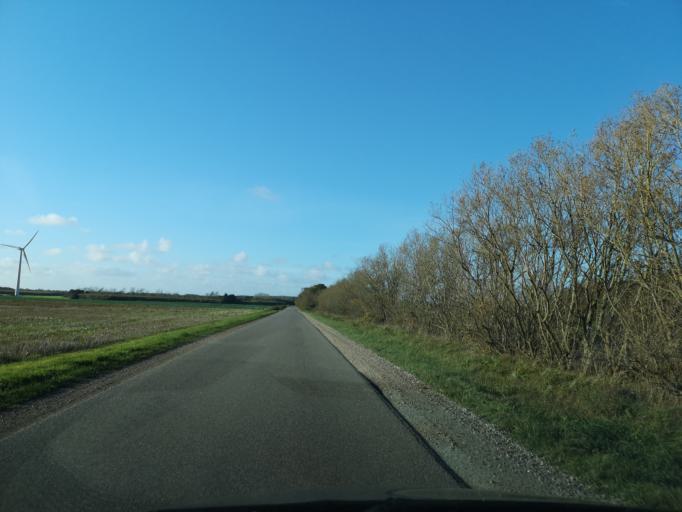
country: DK
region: Central Jutland
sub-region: Ringkobing-Skjern Kommune
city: Tarm
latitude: 55.8118
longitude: 8.4372
